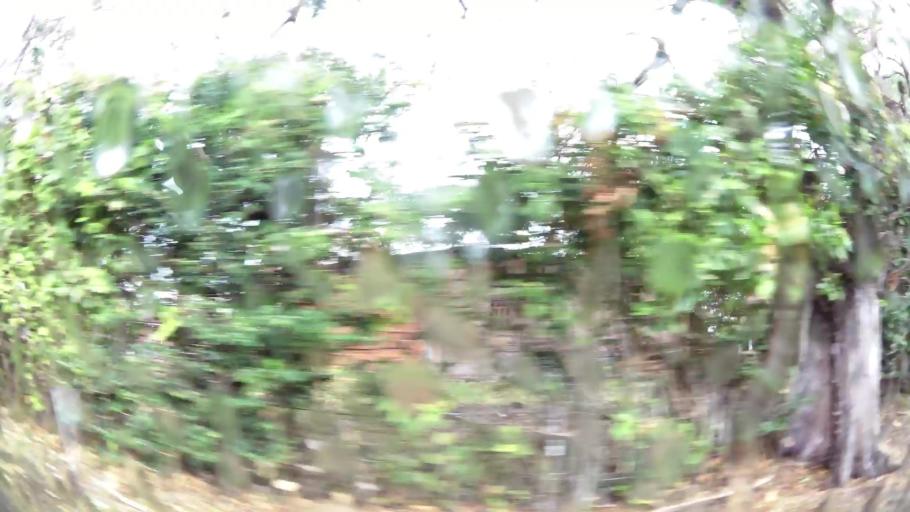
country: MQ
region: Martinique
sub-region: Martinique
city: Les Trois-Ilets
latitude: 14.5396
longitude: -61.0330
